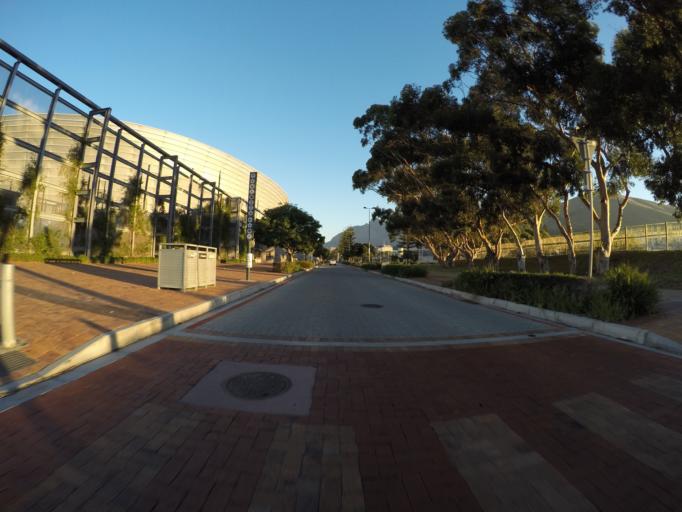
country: ZA
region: Western Cape
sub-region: City of Cape Town
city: Cape Town
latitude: -33.9028
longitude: 18.4084
